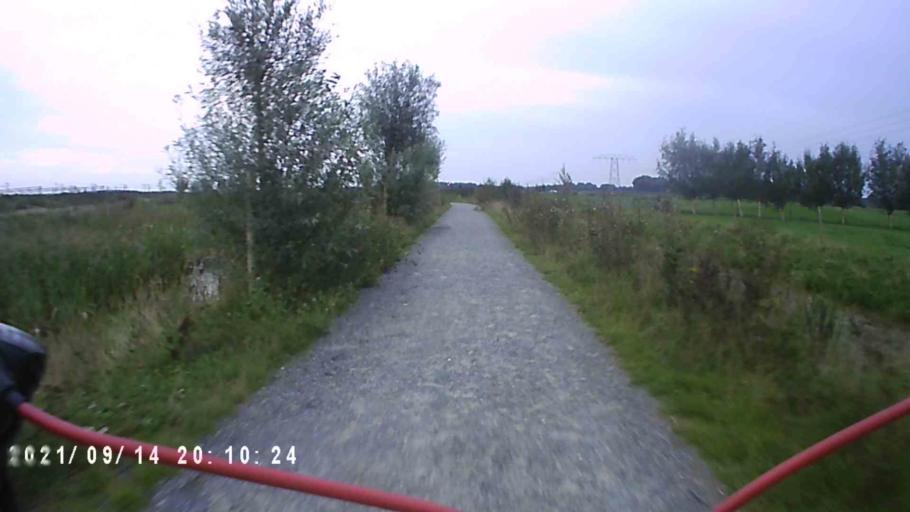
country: NL
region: Groningen
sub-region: Gemeente Haren
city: Haren
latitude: 53.1917
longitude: 6.6127
